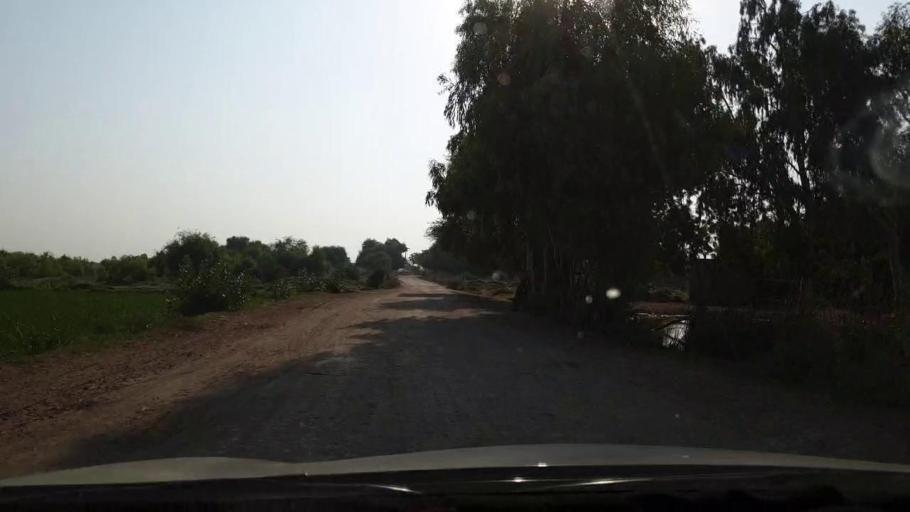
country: PK
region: Sindh
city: Larkana
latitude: 27.5526
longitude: 68.2650
